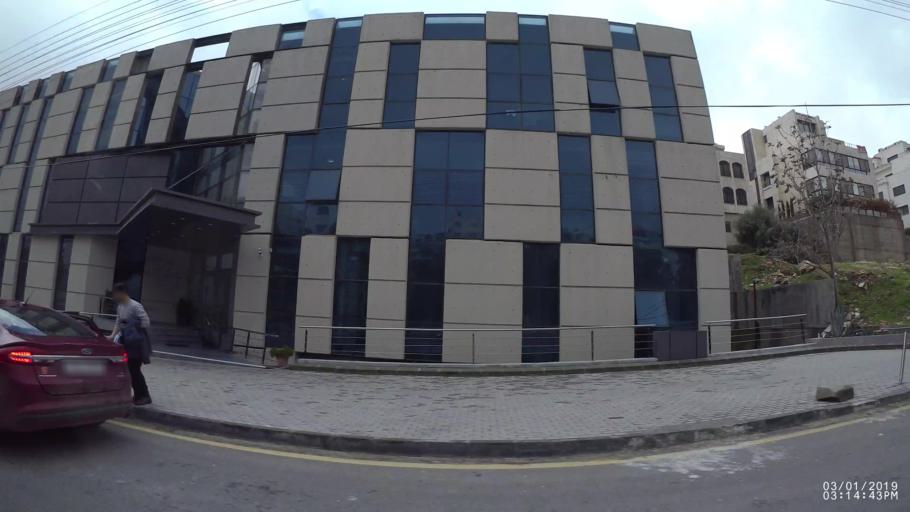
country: JO
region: Amman
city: Amman
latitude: 31.9541
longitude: 35.8874
